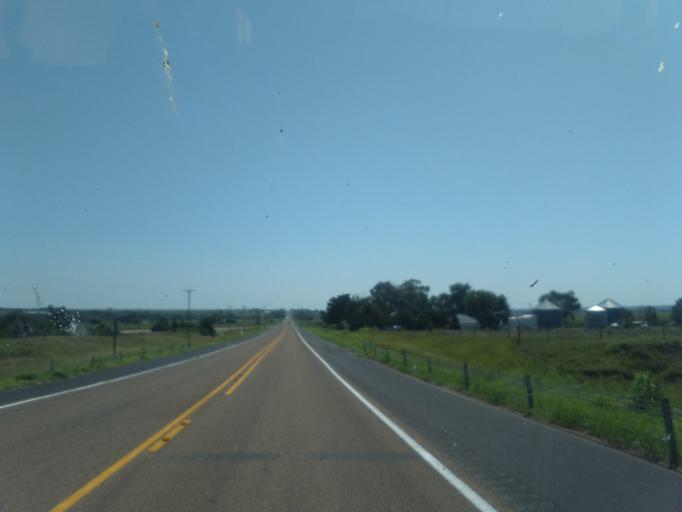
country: US
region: Nebraska
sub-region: Hitchcock County
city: Trenton
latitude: 40.2344
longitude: -100.8988
